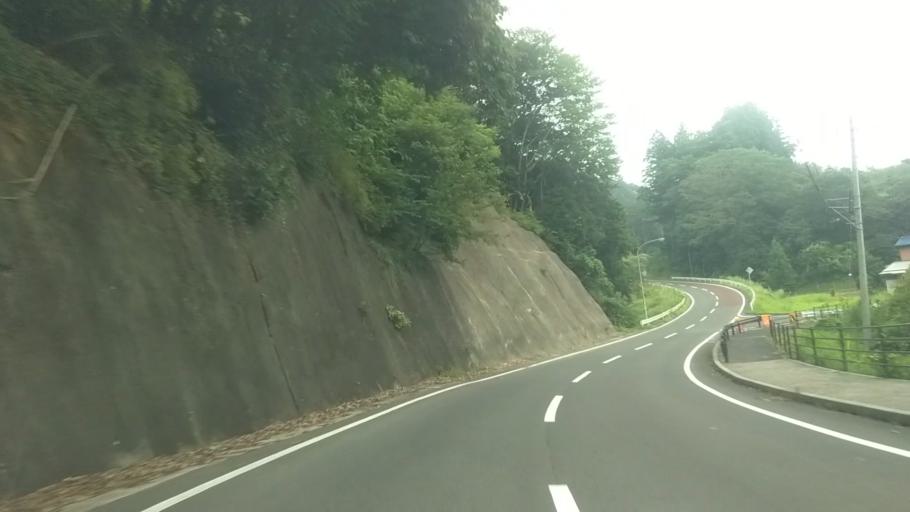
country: JP
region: Chiba
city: Kawaguchi
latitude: 35.2246
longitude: 140.1335
